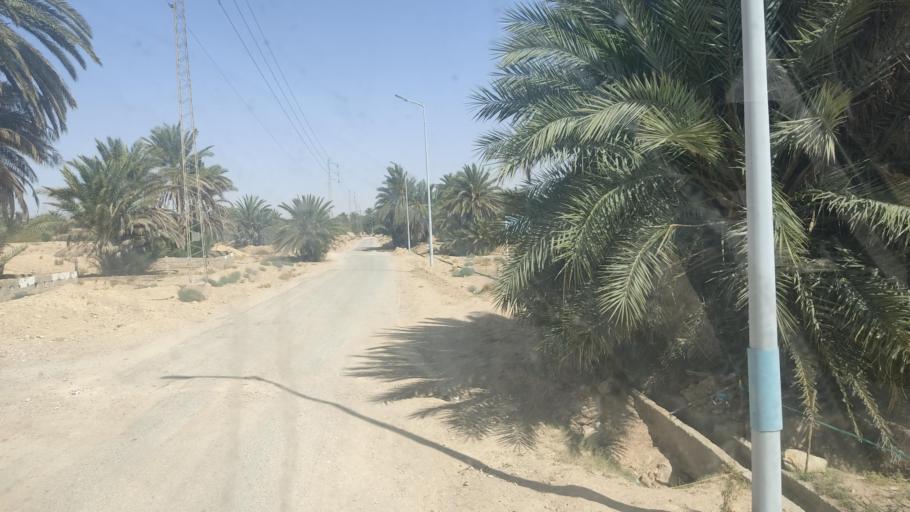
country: TN
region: Gafsa
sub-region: Gafsa Municipality
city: Gafsa
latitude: 34.3358
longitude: 8.9234
